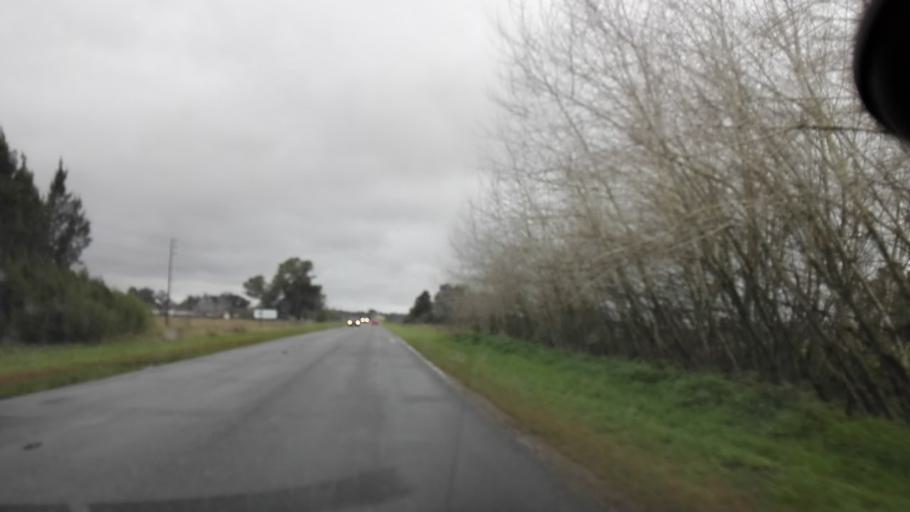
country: AR
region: Buenos Aires
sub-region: Partido de Brandsen
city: Brandsen
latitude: -35.1792
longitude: -58.2714
